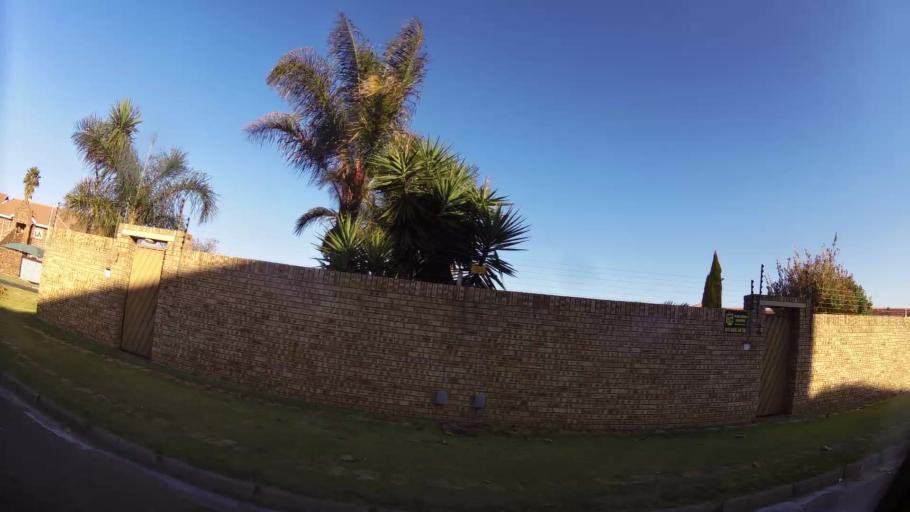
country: ZA
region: Gauteng
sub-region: Ekurhuleni Metropolitan Municipality
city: Germiston
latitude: -26.2877
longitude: 28.1168
